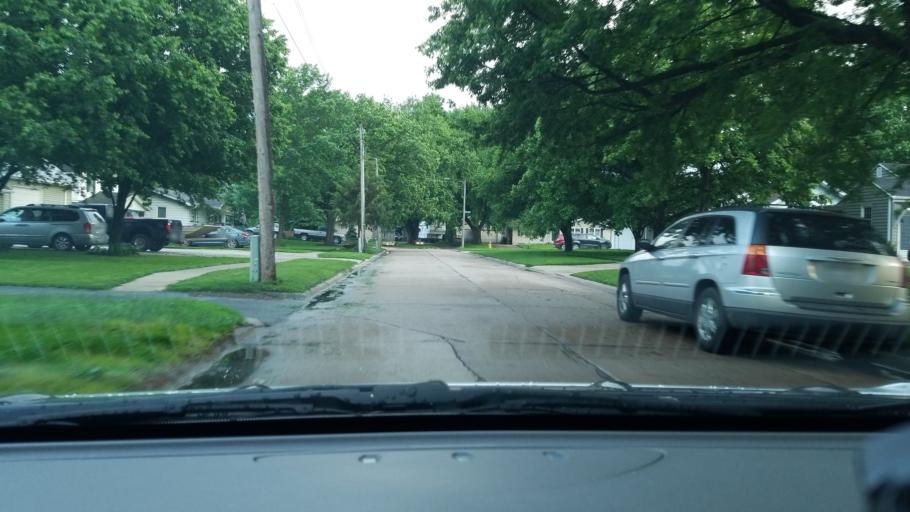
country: US
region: Nebraska
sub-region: Sarpy County
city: Bellevue
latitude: 41.1352
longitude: -95.8895
